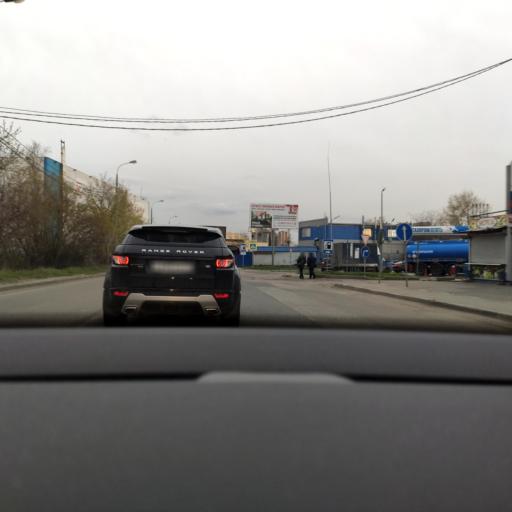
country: RU
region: Moskovskaya
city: Reutov
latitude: 55.7802
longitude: 37.8653
